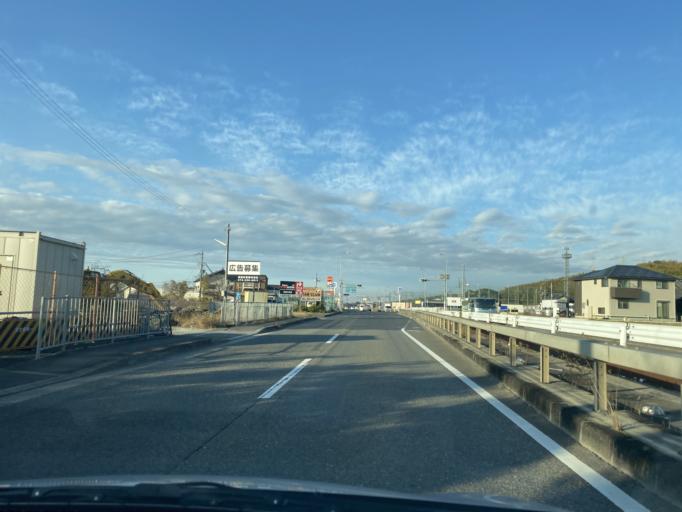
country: JP
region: Osaka
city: Izumi
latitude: 34.4355
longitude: 135.4396
